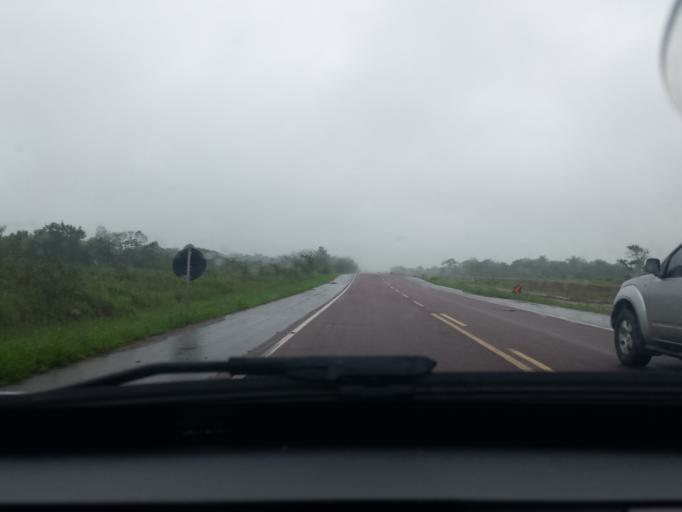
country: BR
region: Santa Catarina
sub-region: Itajai
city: Itajai
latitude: -26.8416
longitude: -48.7928
